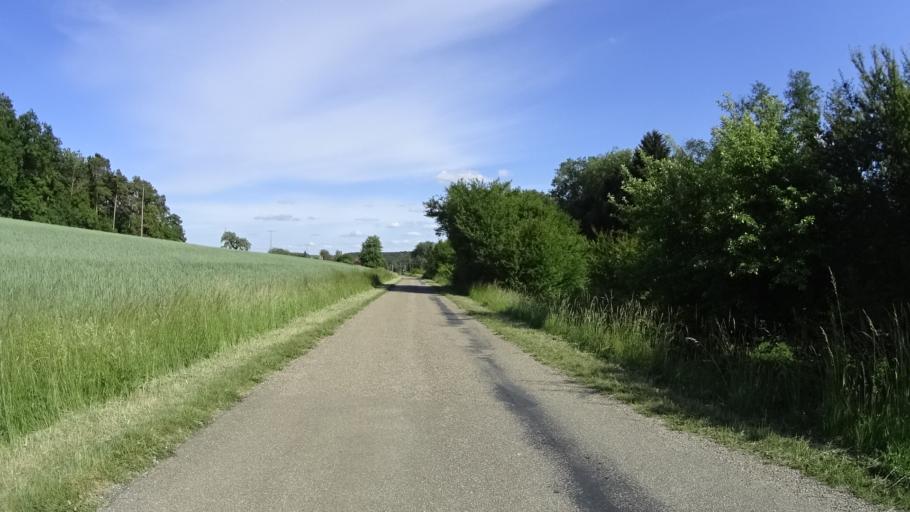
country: DE
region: Baden-Wuerttemberg
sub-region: Regierungsbezirk Stuttgart
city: Buch am Ahorn
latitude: 49.5229
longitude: 9.5813
